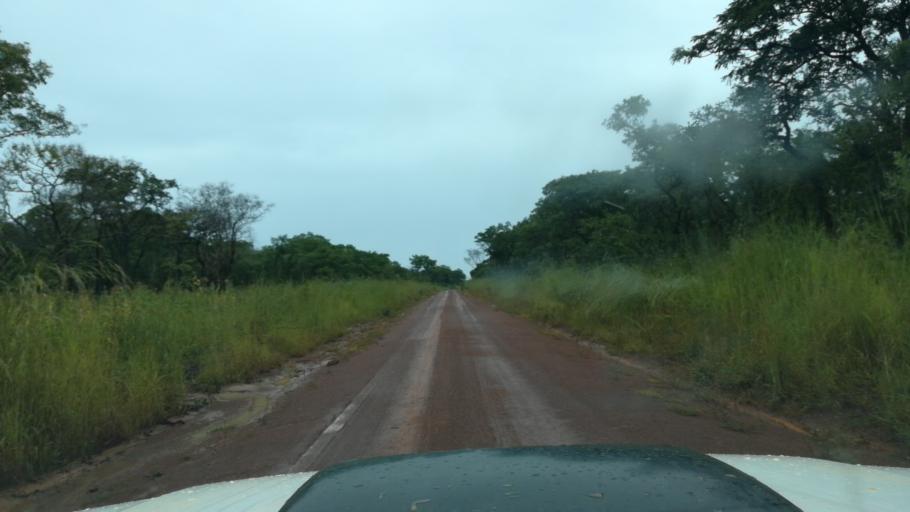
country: ZM
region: Luapula
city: Mwense
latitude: -10.3530
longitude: 28.1076
